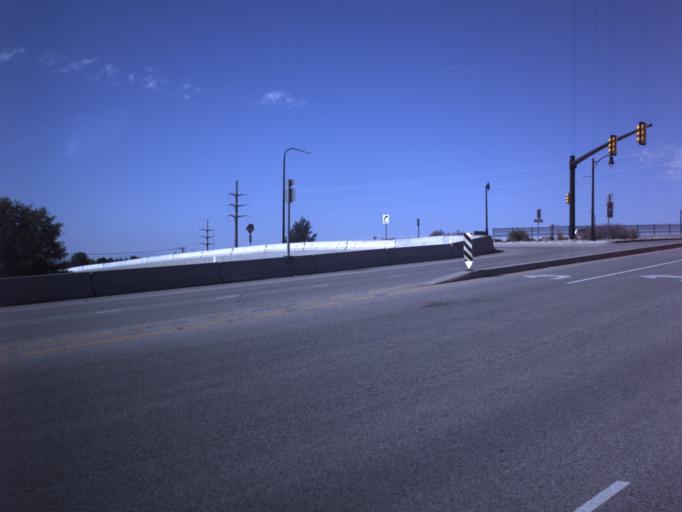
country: US
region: Utah
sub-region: Davis County
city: Layton
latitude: 41.0563
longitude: -111.9593
